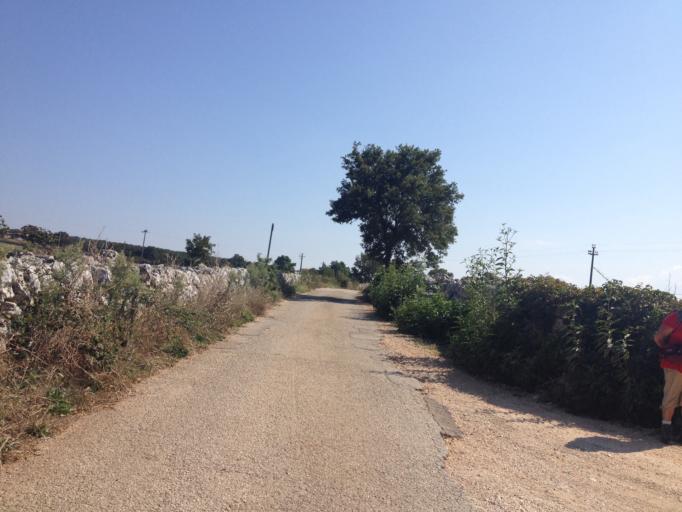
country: IT
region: Apulia
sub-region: Provincia di Bari
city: Noci
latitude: 40.8081
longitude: 17.1752
